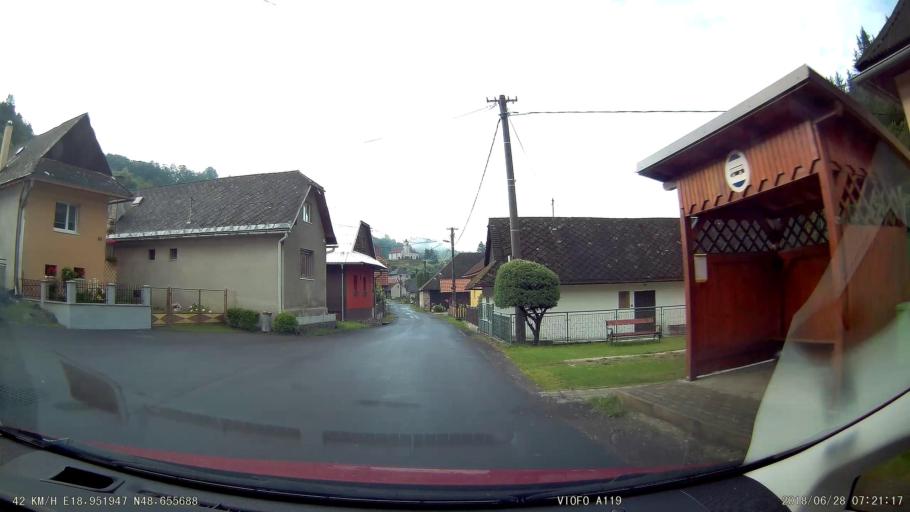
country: SK
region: Banskobystricky
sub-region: Okres Ziar nad Hronom
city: Kremnica
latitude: 48.6554
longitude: 18.9521
